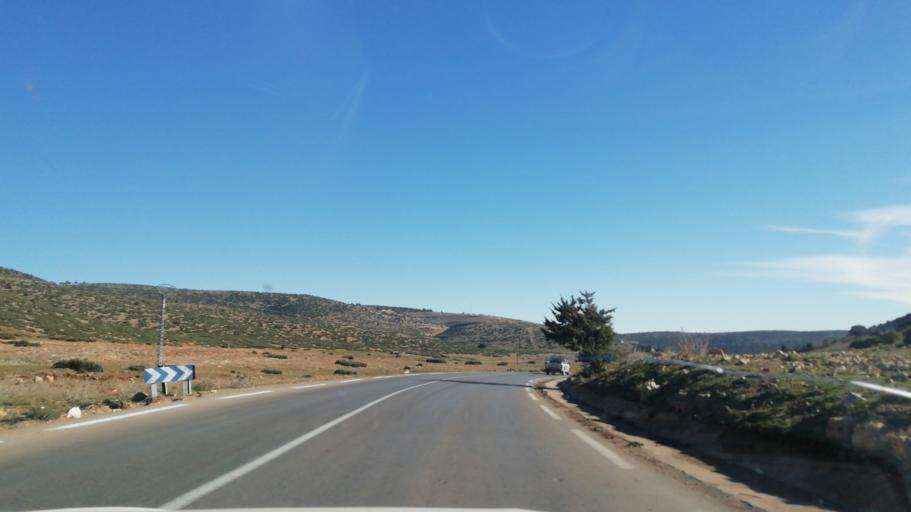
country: DZ
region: Tlemcen
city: Sebdou
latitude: 34.7143
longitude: -1.3265
